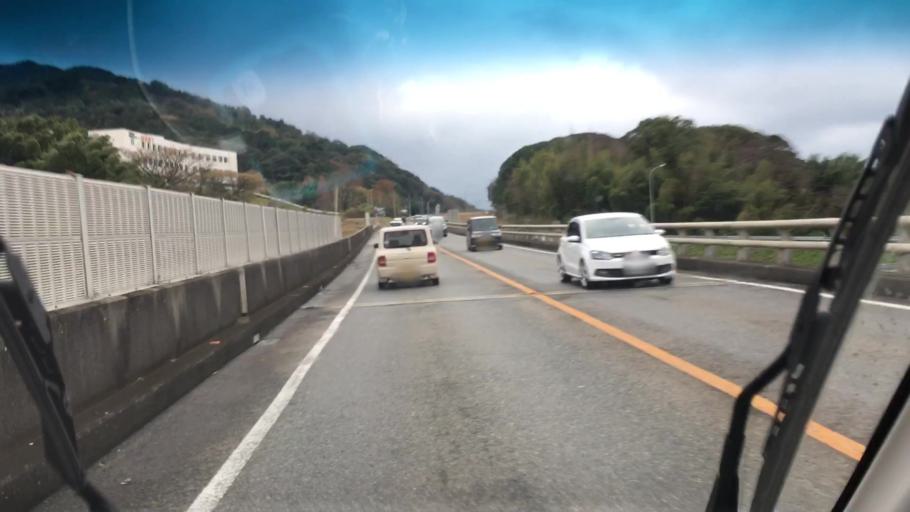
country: JP
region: Fukuoka
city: Maebaru-chuo
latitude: 33.5115
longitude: 130.1338
